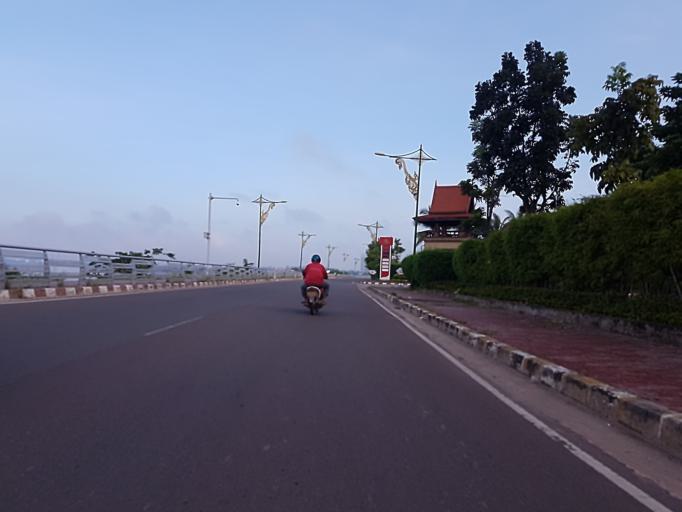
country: LA
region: Vientiane
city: Vientiane
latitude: 17.9434
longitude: 102.6164
